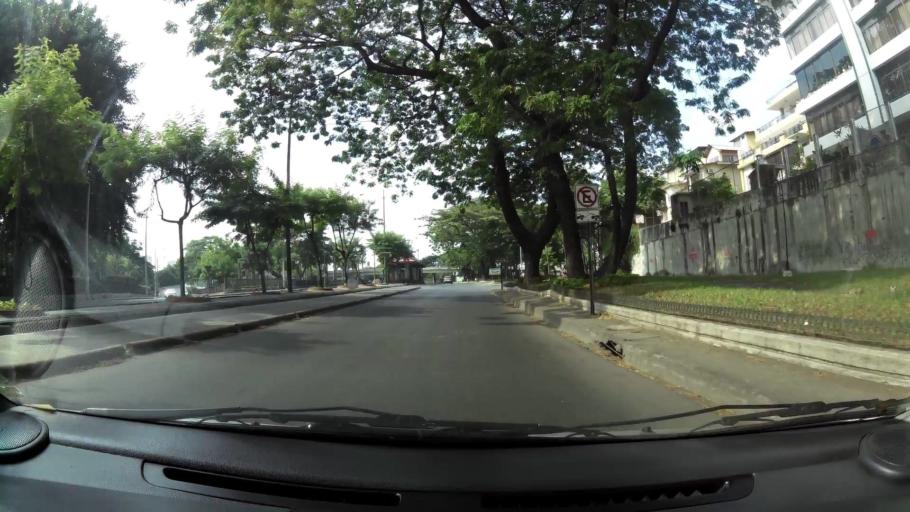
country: EC
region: Guayas
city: Guayaquil
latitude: -2.1841
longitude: -79.9010
